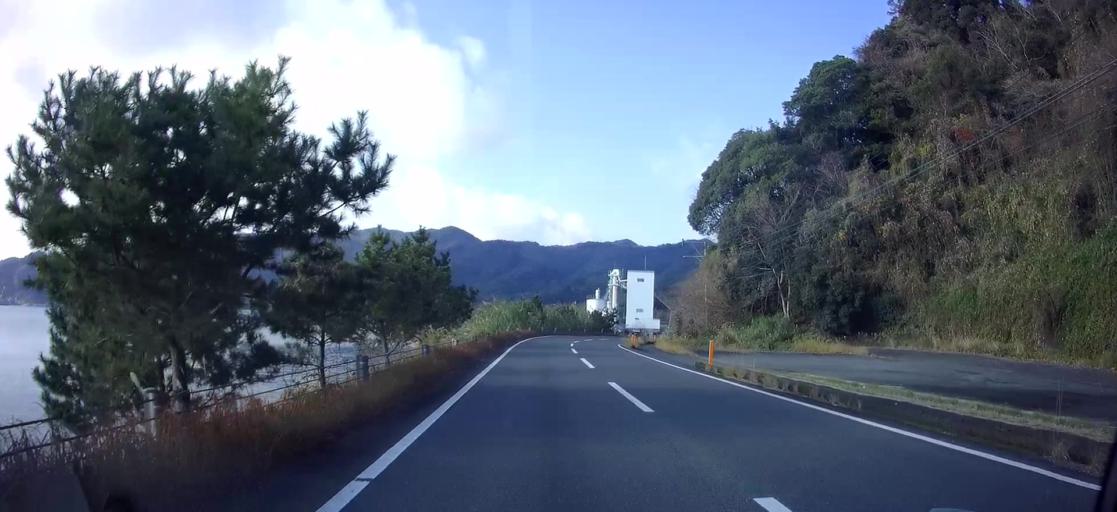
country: JP
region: Kumamoto
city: Minamata
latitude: 32.3866
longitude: 130.3781
